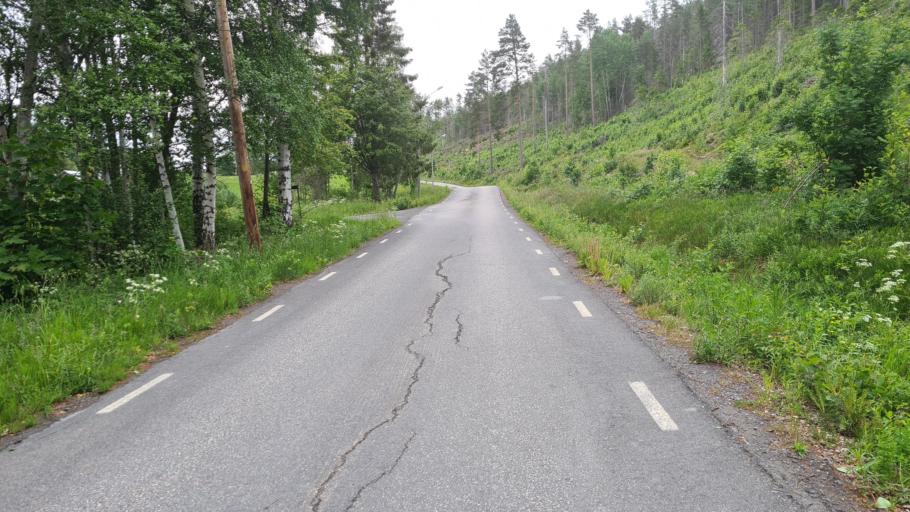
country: SE
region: Vaesternorrland
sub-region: Kramfors Kommun
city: Nordingra
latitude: 62.9765
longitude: 18.4267
